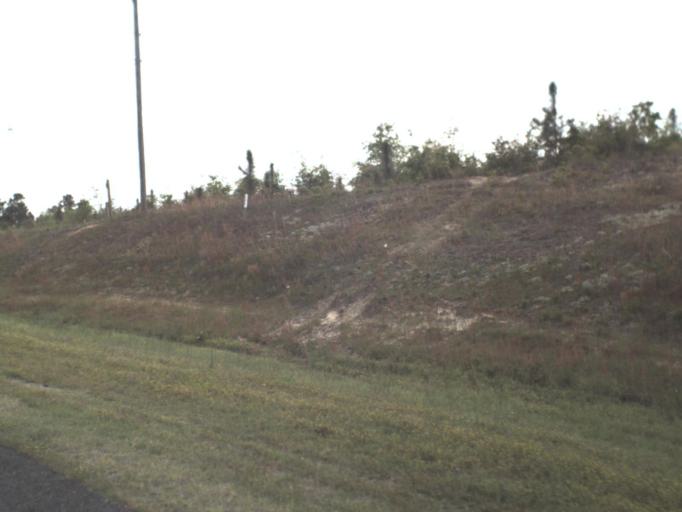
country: US
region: Florida
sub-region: Escambia County
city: Molino
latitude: 30.7673
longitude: -87.3409
